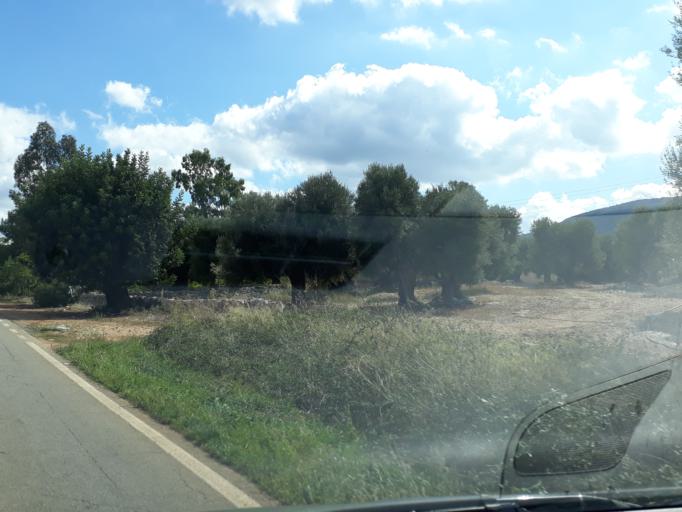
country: IT
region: Apulia
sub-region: Provincia di Brindisi
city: Pezze di Greco
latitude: 40.7996
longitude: 17.4063
